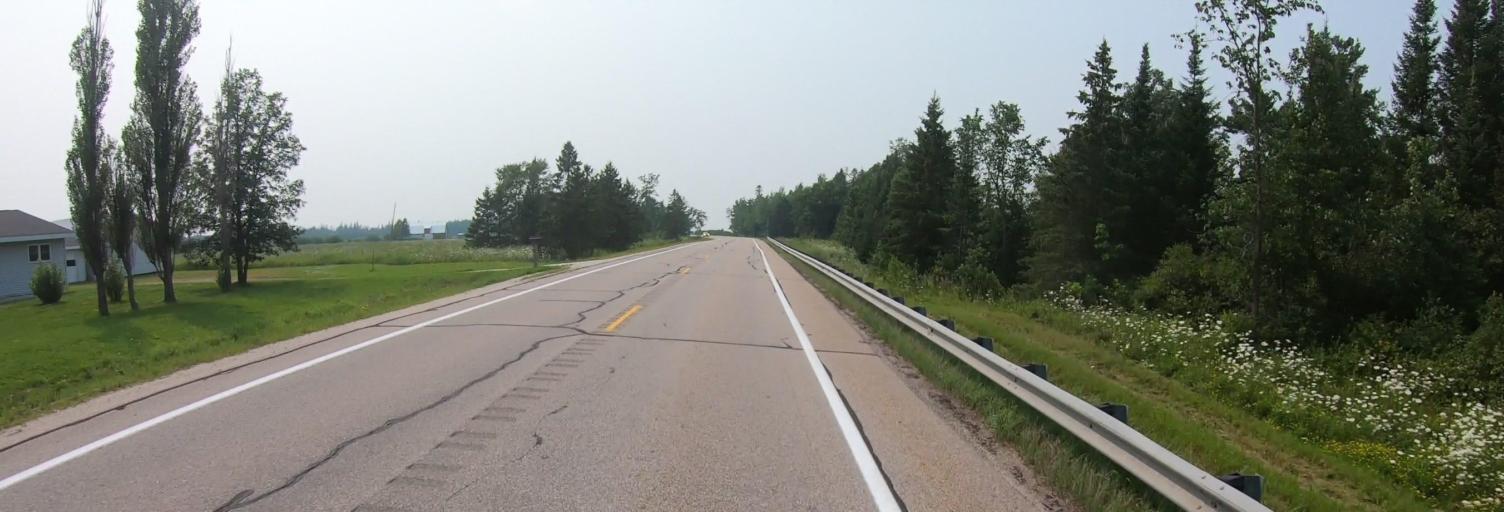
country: US
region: Michigan
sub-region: Chippewa County
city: Sault Ste. Marie
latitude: 46.1286
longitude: -84.3327
